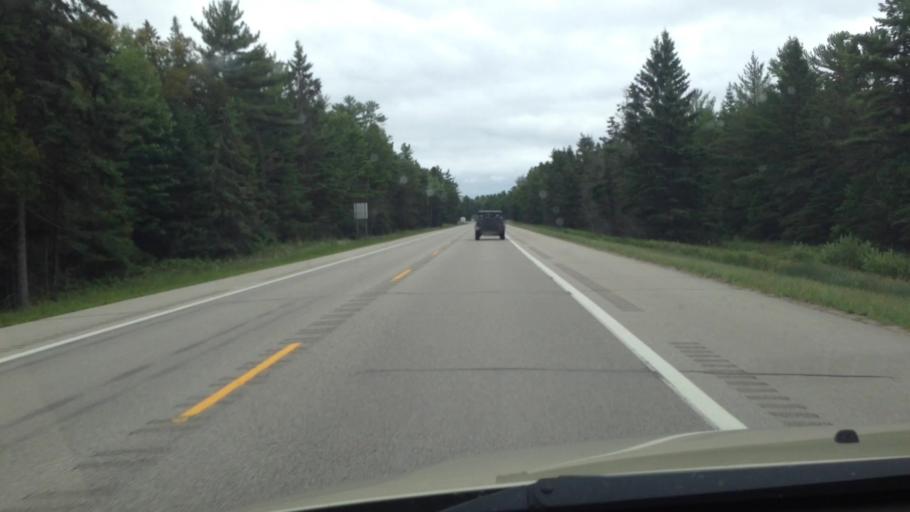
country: US
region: Michigan
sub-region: Luce County
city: Newberry
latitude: 46.0700
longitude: -85.2716
